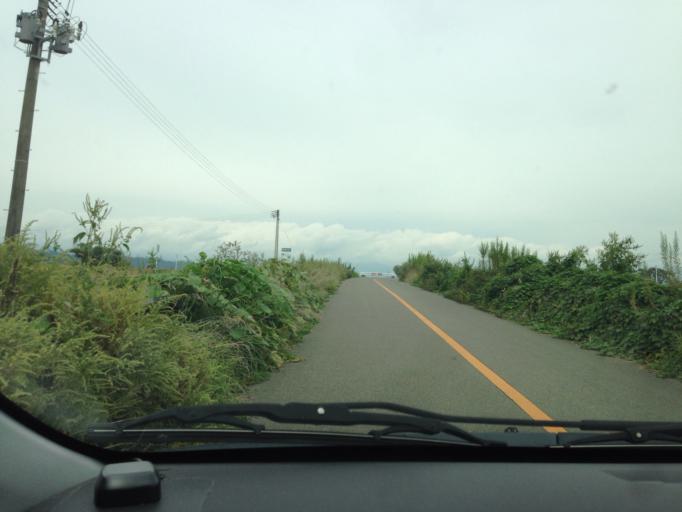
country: JP
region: Fukushima
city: Kitakata
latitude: 37.5927
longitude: 139.8352
